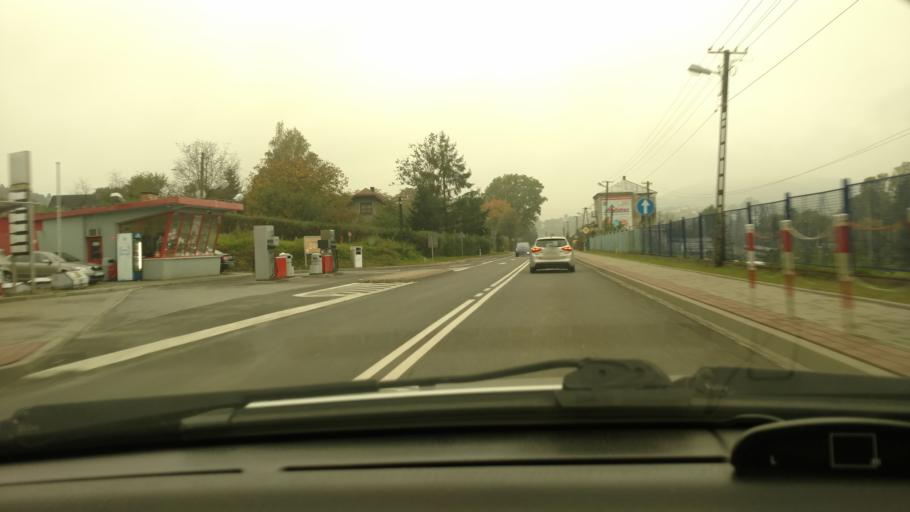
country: PL
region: Lesser Poland Voivodeship
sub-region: Powiat nowosadecki
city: Grybow
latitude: 49.6250
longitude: 20.9569
